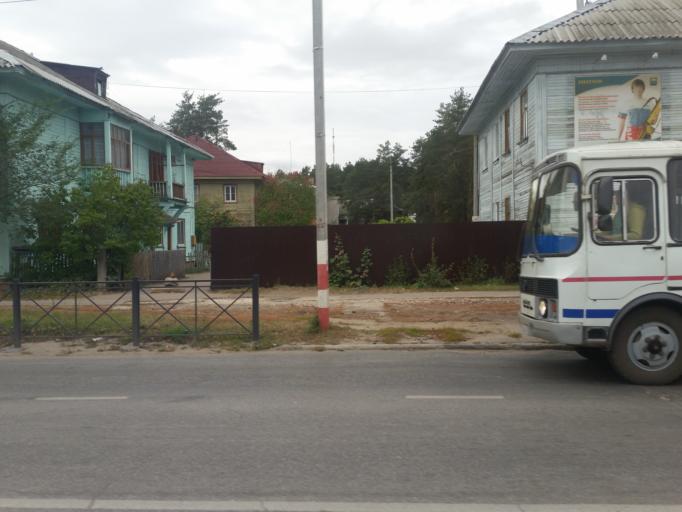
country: RU
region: Ulyanovsk
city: Dimitrovgrad
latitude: 54.2350
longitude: 49.5702
